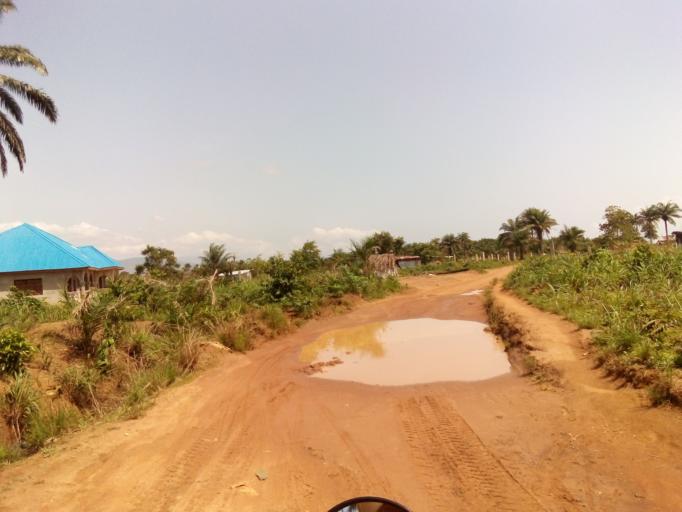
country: SL
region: Western Area
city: Waterloo
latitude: 8.3418
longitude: -13.0111
